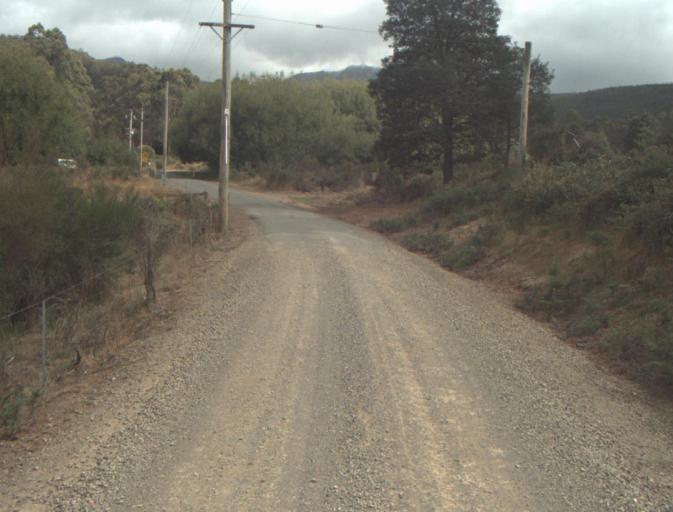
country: AU
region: Tasmania
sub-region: Northern Midlands
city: Evandale
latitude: -41.4501
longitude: 147.4797
